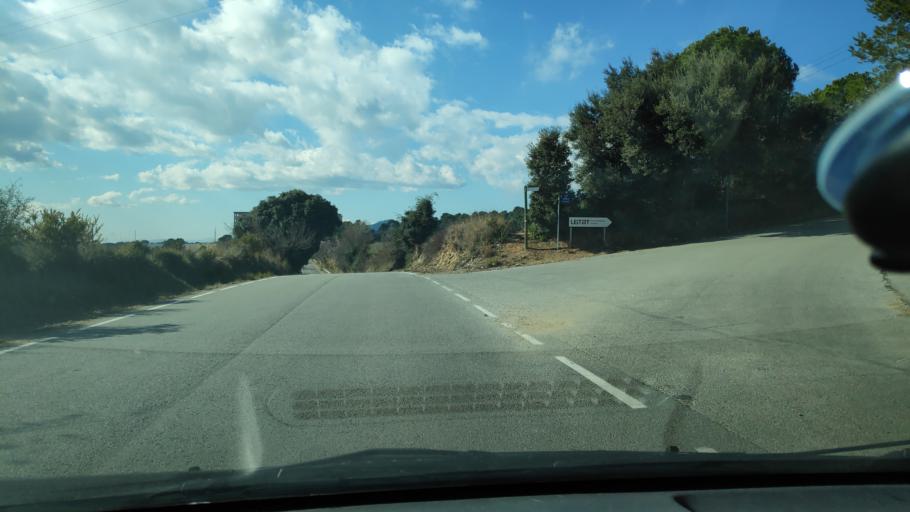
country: ES
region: Catalonia
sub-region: Provincia de Barcelona
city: Matadepera
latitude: 41.5962
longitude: 2.0140
